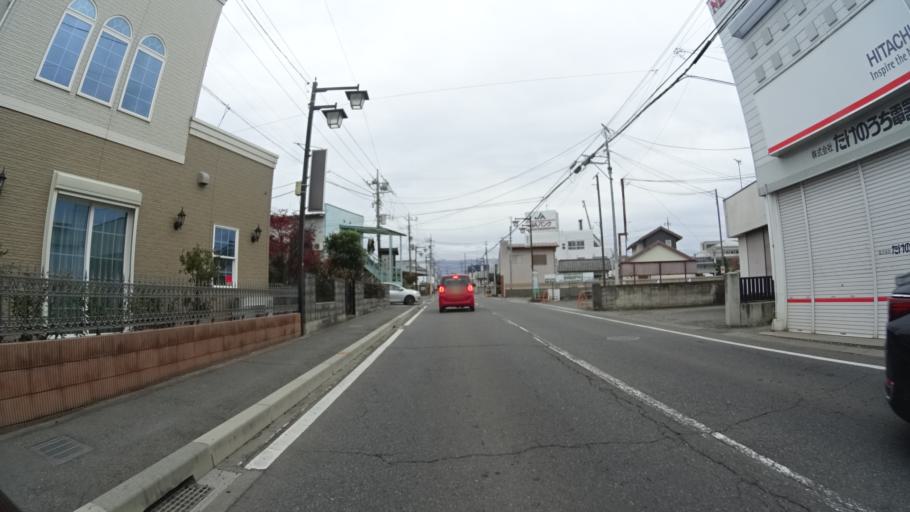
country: JP
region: Gunma
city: Numata
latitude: 36.6490
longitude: 139.0568
